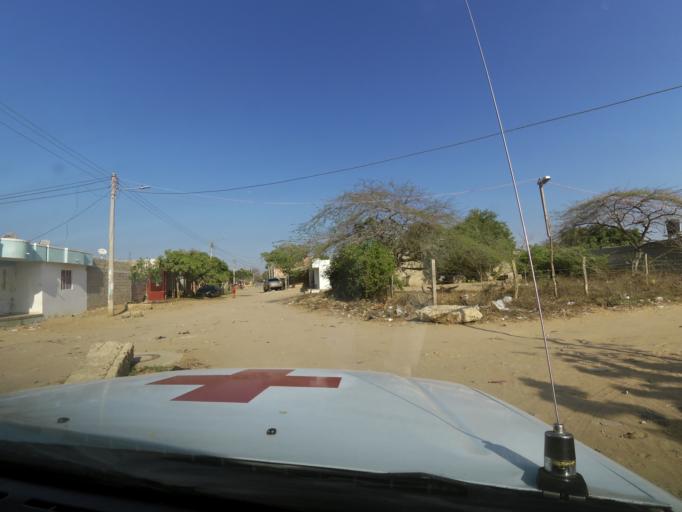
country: CO
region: La Guajira
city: Riohacha
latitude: 11.5239
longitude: -72.9167
